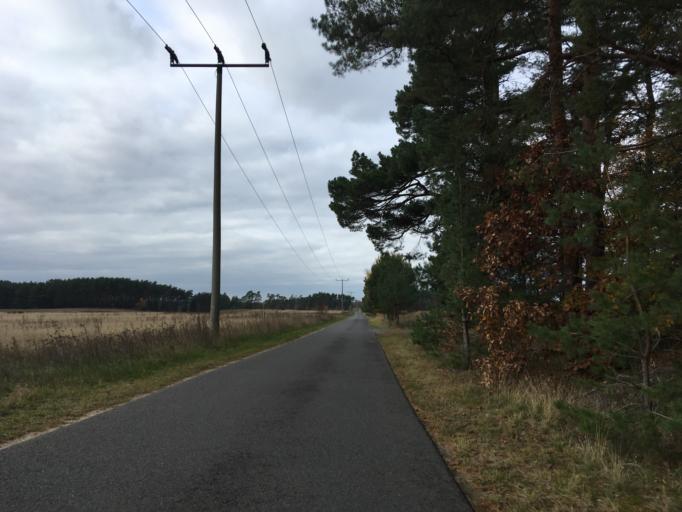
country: DE
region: Brandenburg
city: Jamlitz
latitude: 52.0809
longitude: 14.4519
